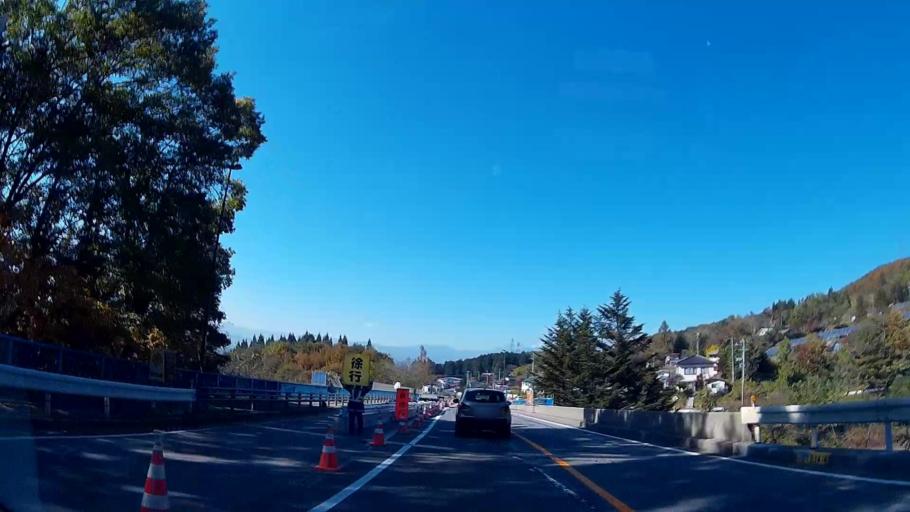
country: JP
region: Nagano
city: Okaya
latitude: 36.0923
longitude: 138.0208
